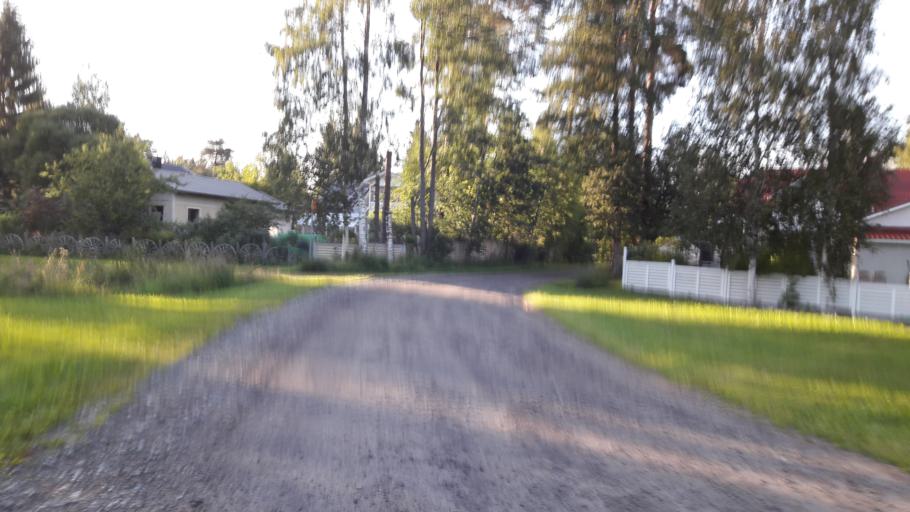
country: FI
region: North Karelia
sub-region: Joensuu
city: Joensuu
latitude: 62.6135
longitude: 29.7078
